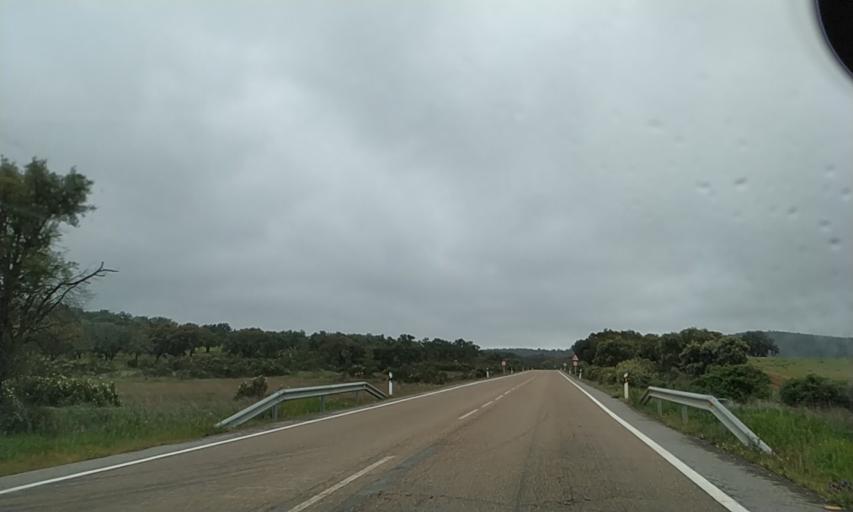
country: ES
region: Extremadura
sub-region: Provincia de Caceres
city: Malpartida de Caceres
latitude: 39.2974
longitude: -6.5184
